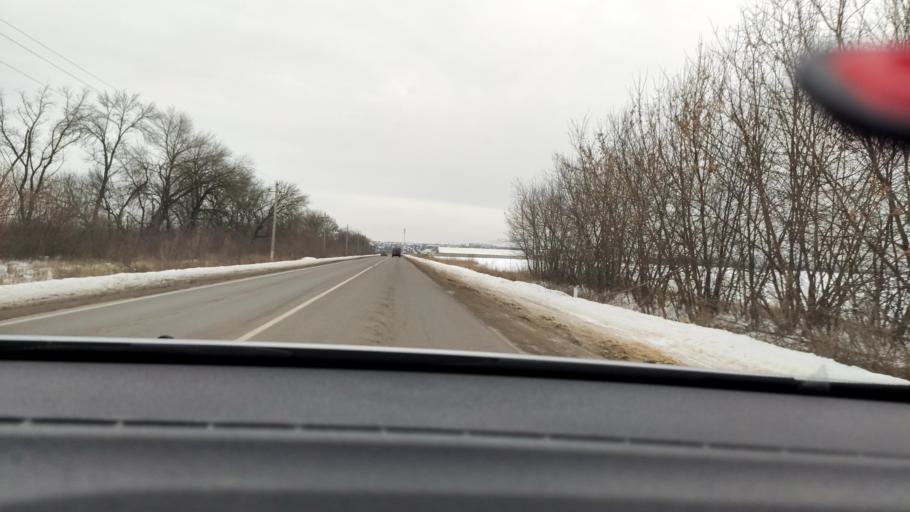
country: RU
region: Voronezj
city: Semiluki
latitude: 51.7273
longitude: 38.9874
